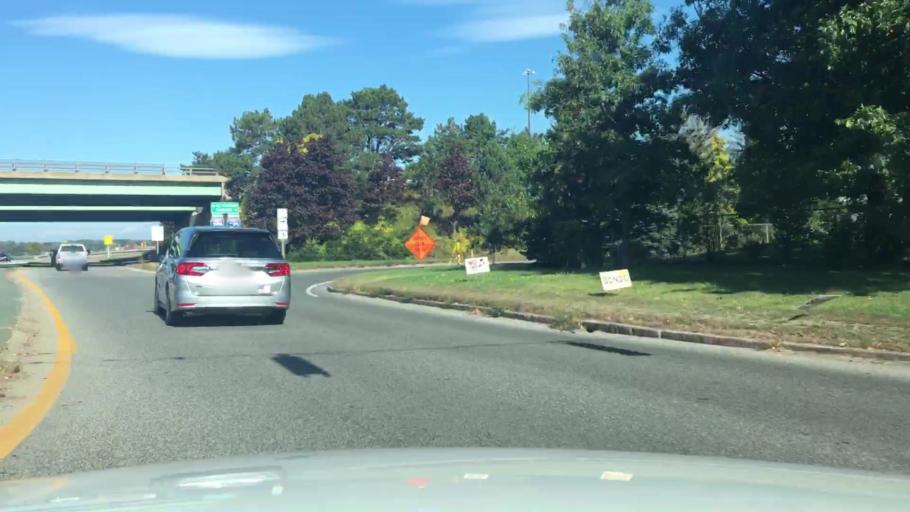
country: US
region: Maine
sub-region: Cumberland County
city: Portland
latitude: 43.6653
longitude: -70.2601
